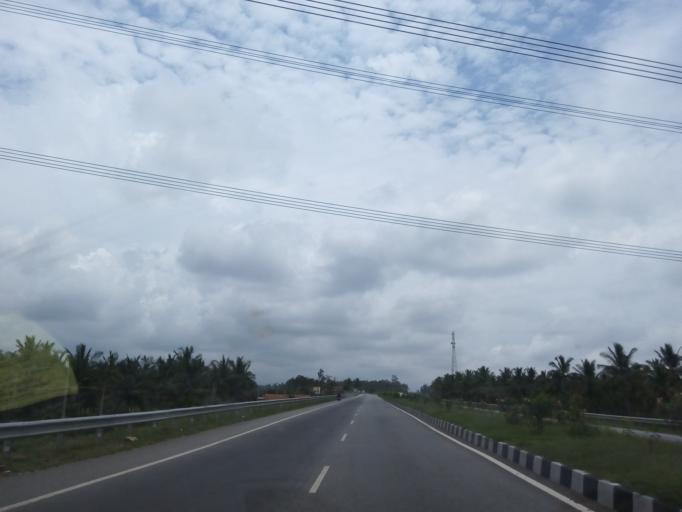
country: IN
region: Karnataka
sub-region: Hassan
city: Hassan
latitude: 12.9905
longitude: 76.1879
